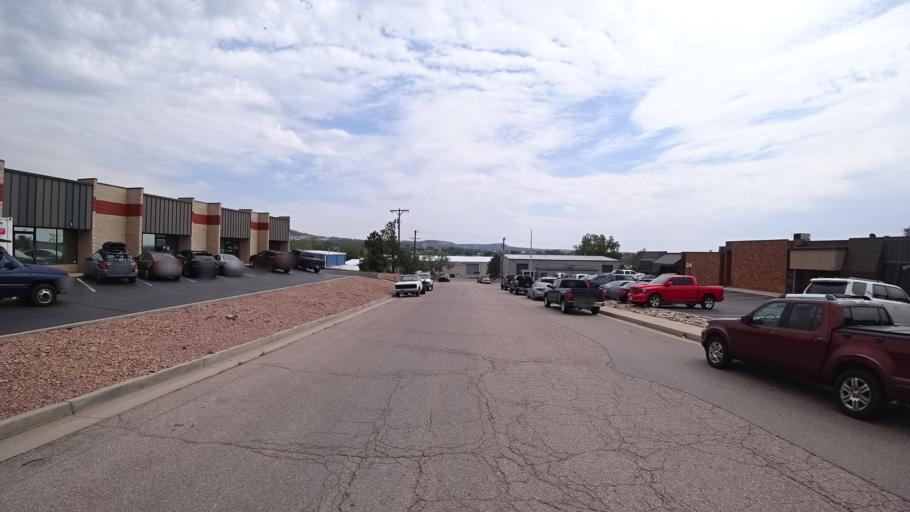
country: US
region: Colorado
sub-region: El Paso County
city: Colorado Springs
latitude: 38.8899
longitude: -104.8318
